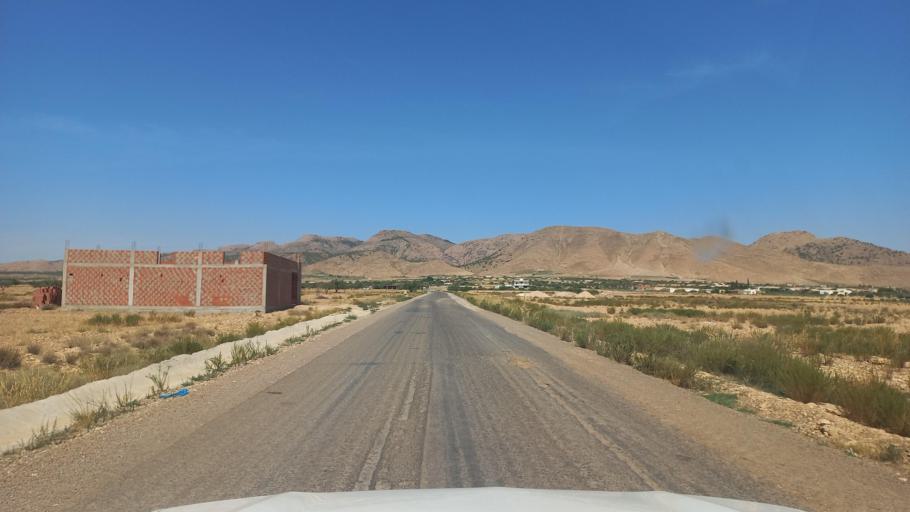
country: TN
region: Al Qasrayn
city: Sbiba
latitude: 35.4387
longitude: 9.0778
